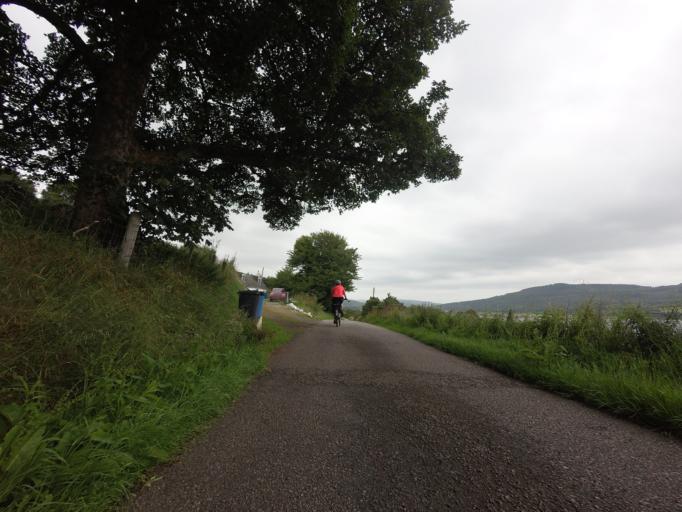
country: GB
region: Scotland
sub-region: Highland
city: Evanton
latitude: 57.8995
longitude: -4.3813
